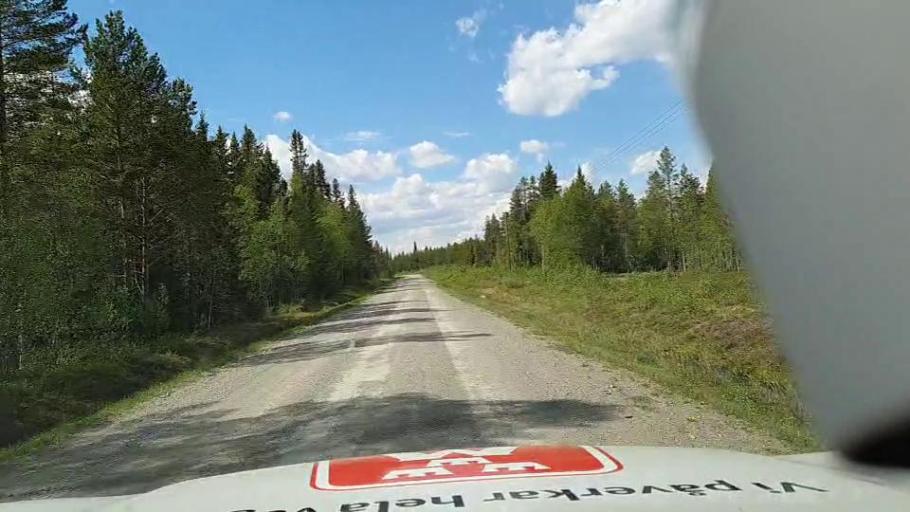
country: SE
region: Vaesterbotten
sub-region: Vilhelmina Kommun
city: Sjoberg
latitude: 64.5438
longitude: 15.6486
